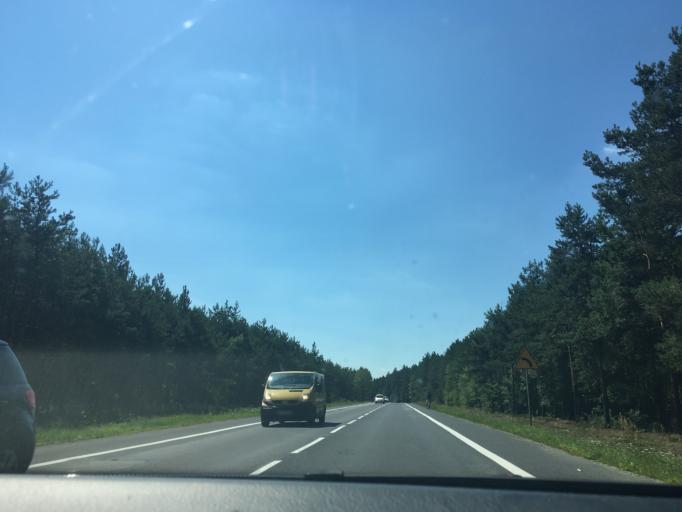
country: PL
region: Subcarpathian Voivodeship
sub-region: Powiat nizanski
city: Jarocin
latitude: 50.6036
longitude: 22.2778
